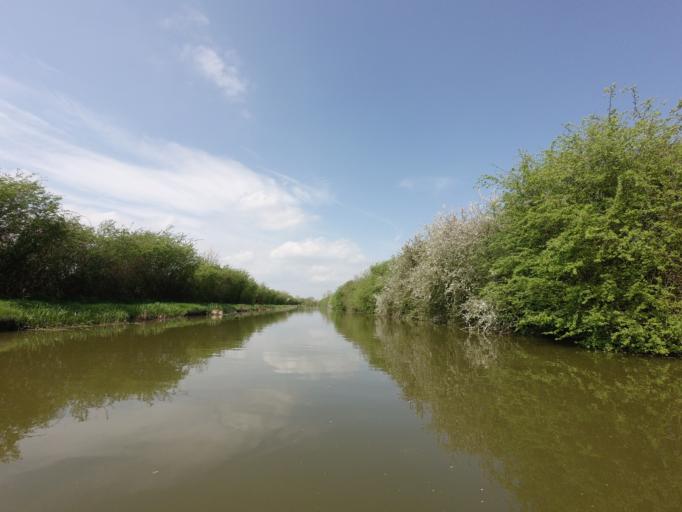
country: GB
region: England
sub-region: Buckinghamshire
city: Cheddington
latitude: 51.8762
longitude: -0.6558
